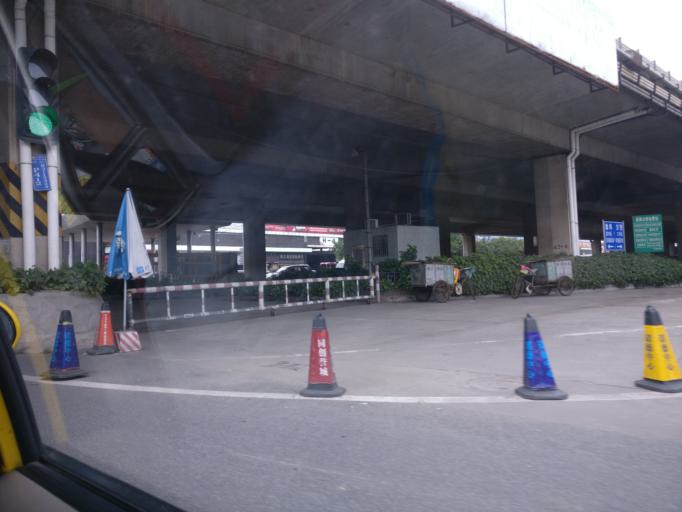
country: CN
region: Guangdong
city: Xiaoguwei
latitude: 23.0371
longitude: 113.3334
